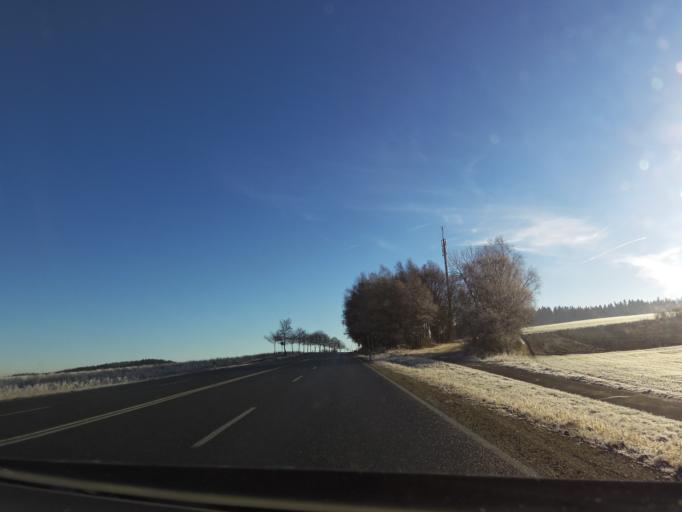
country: DE
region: Bavaria
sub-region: Upper Franconia
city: Bad Alexandersbad
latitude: 50.0184
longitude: 12.0374
